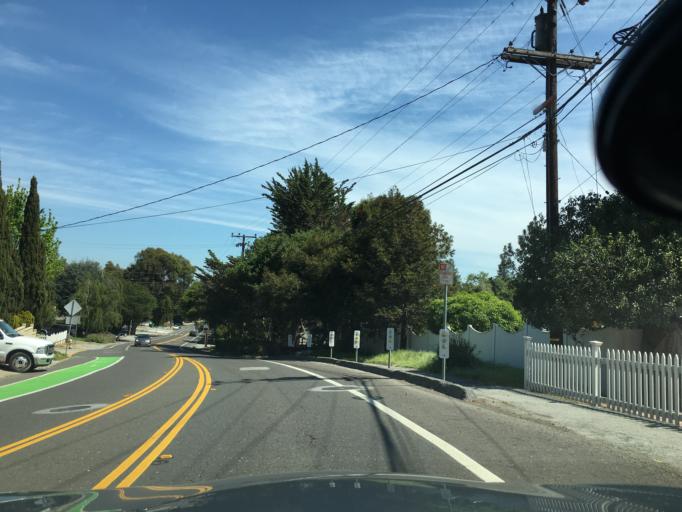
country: US
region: California
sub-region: San Mateo County
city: San Carlos
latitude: 37.5021
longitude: -122.2754
